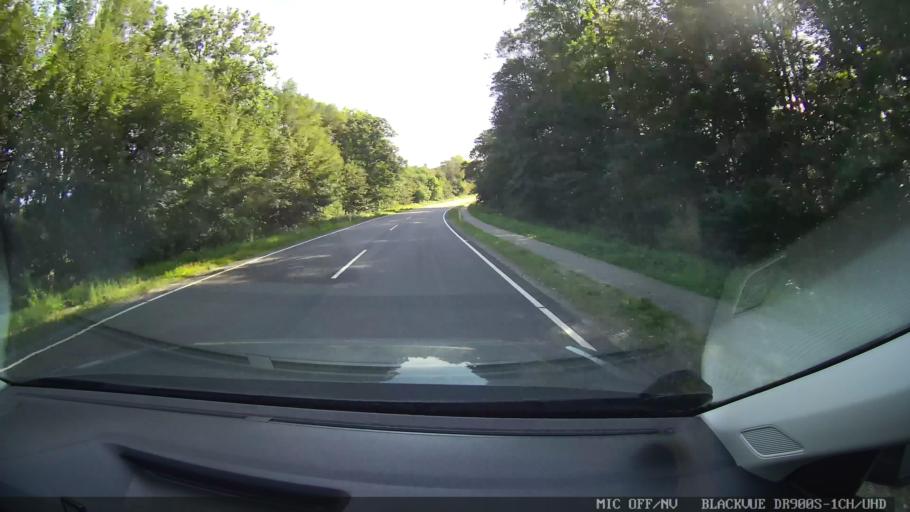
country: DK
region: North Denmark
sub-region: Mariagerfjord Kommune
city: Arden
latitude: 56.7837
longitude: 9.7276
